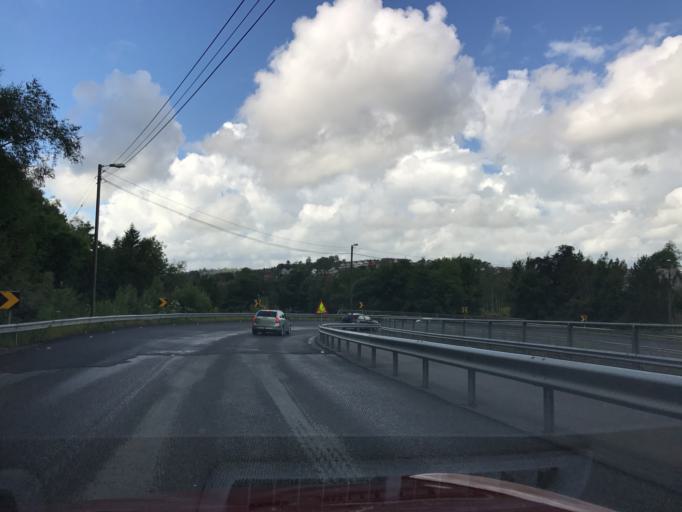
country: NO
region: Hordaland
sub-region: Bergen
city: Sandsli
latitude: 60.3048
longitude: 5.3641
